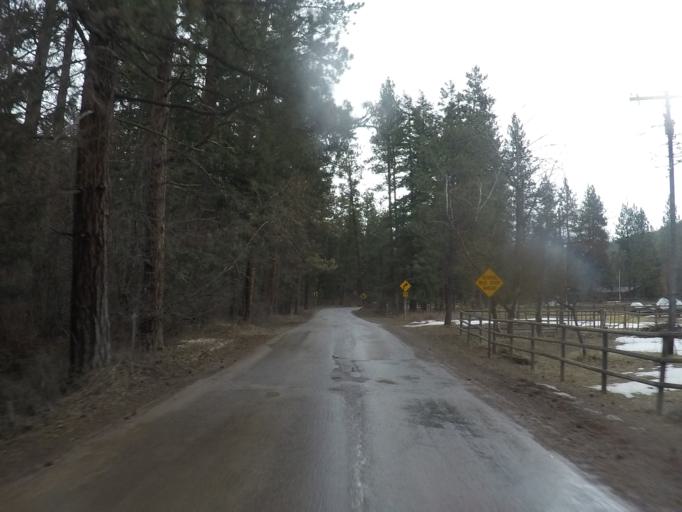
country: US
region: Montana
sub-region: Missoula County
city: East Missoula
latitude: 46.9195
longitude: -113.9598
